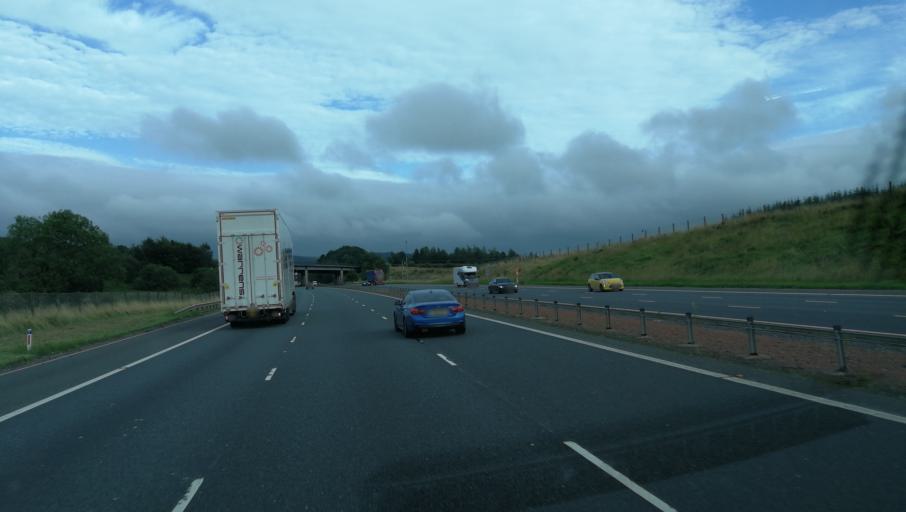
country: GB
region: Scotland
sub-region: Dumfries and Galloway
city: Lockerbie
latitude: 55.0998
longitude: -3.3405
